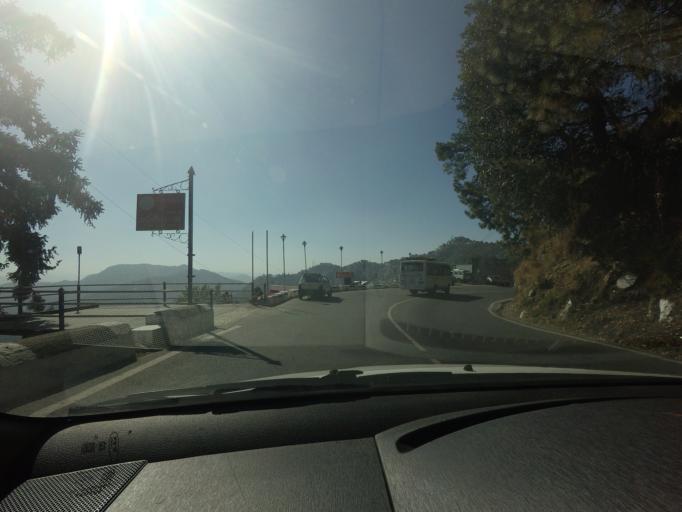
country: IN
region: Himachal Pradesh
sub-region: Shimla
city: Shimla
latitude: 31.1013
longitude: 77.1485
